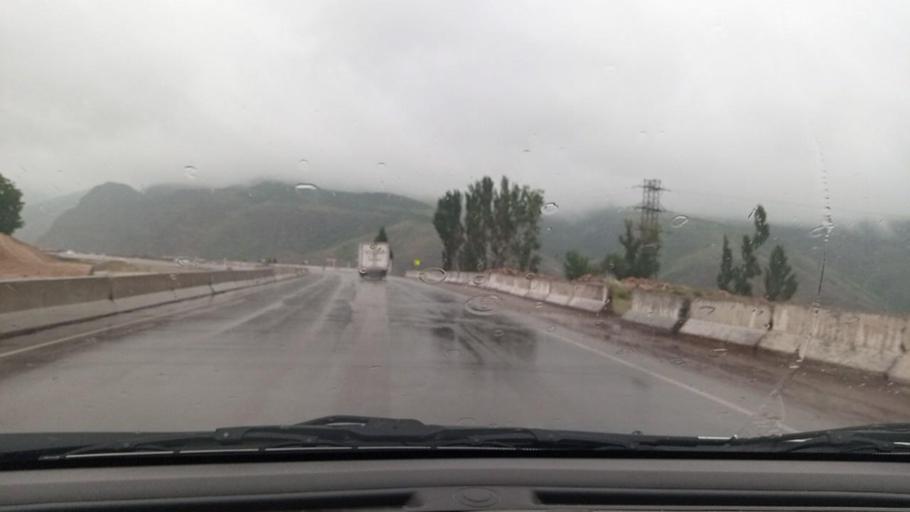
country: UZ
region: Toshkent
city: Angren
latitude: 41.0697
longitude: 70.2376
